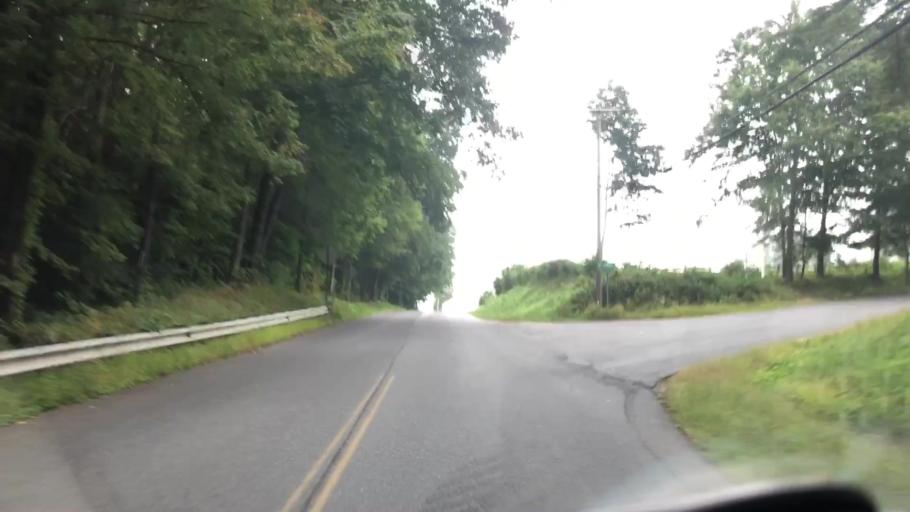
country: US
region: Massachusetts
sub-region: Franklin County
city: Northfield
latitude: 42.6756
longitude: -72.4812
